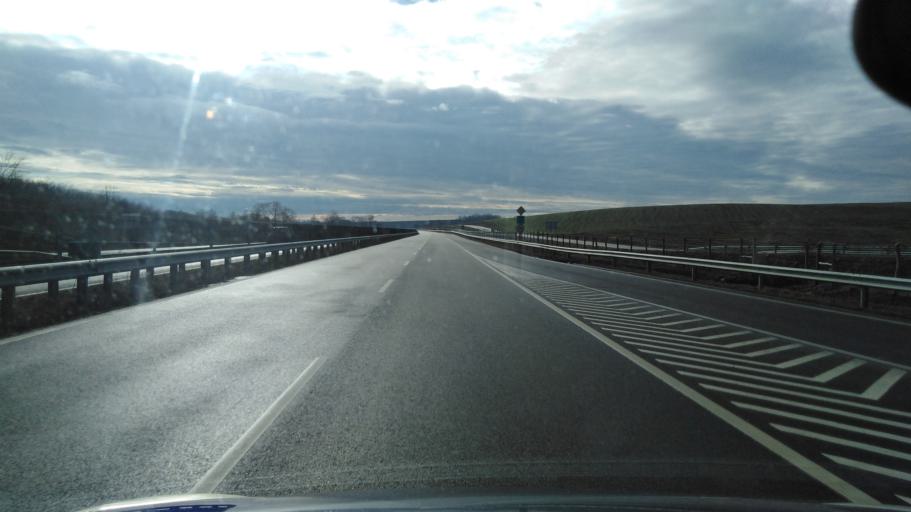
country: HU
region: Nograd
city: Paszto
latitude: 47.8989
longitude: 19.6738
